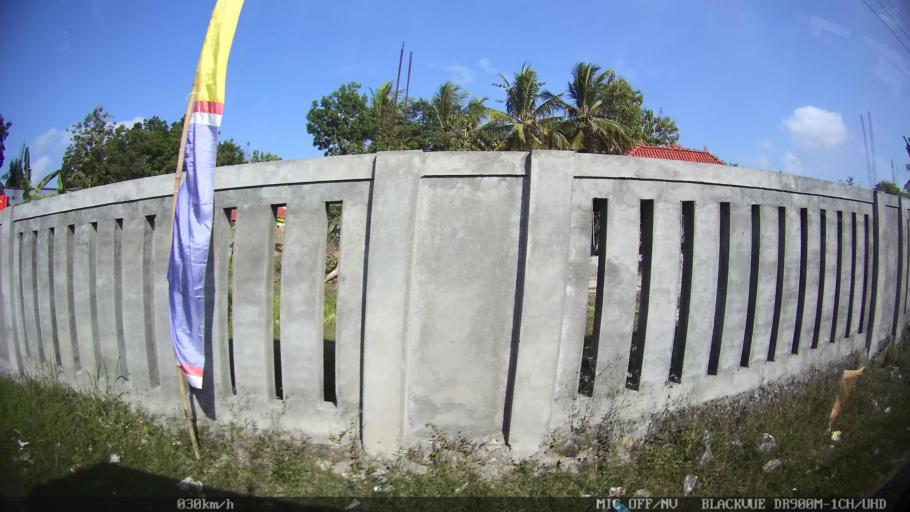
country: ID
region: Daerah Istimewa Yogyakarta
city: Kasihan
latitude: -7.8229
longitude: 110.2922
